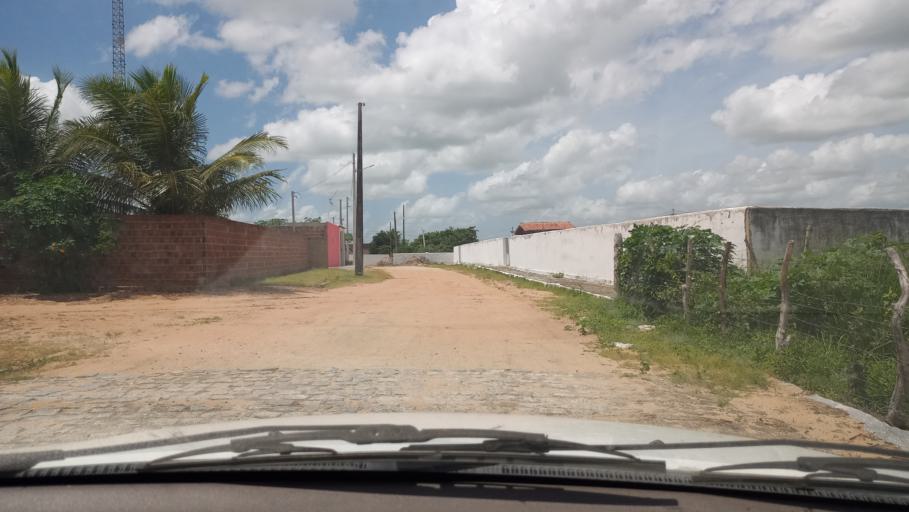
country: BR
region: Rio Grande do Norte
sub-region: Brejinho
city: Brejinho
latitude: -6.2696
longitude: -35.3741
